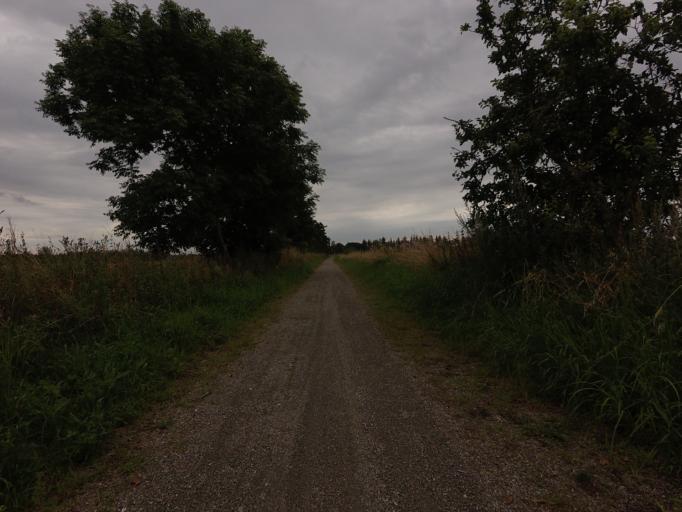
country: DK
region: North Denmark
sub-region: Alborg Kommune
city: Vadum
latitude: 57.1033
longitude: 9.8925
